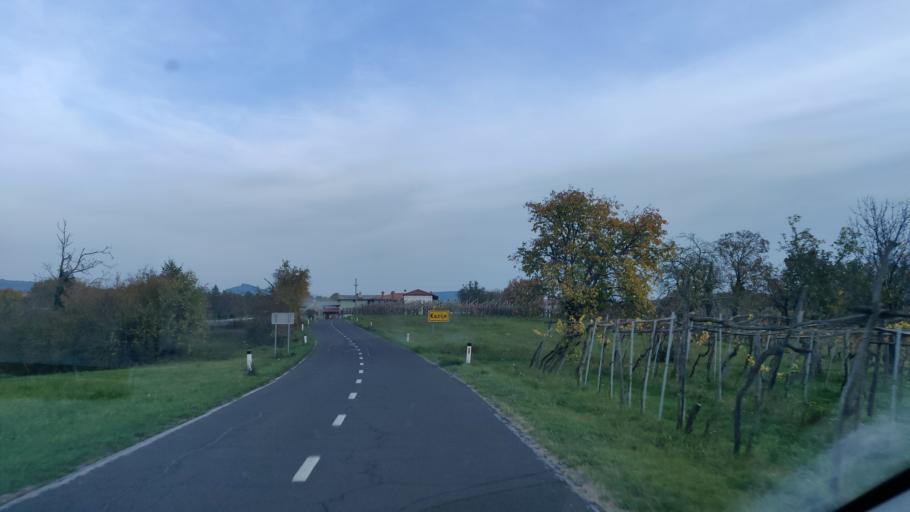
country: SI
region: Sezana
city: Sezana
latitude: 45.7626
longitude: 13.9028
